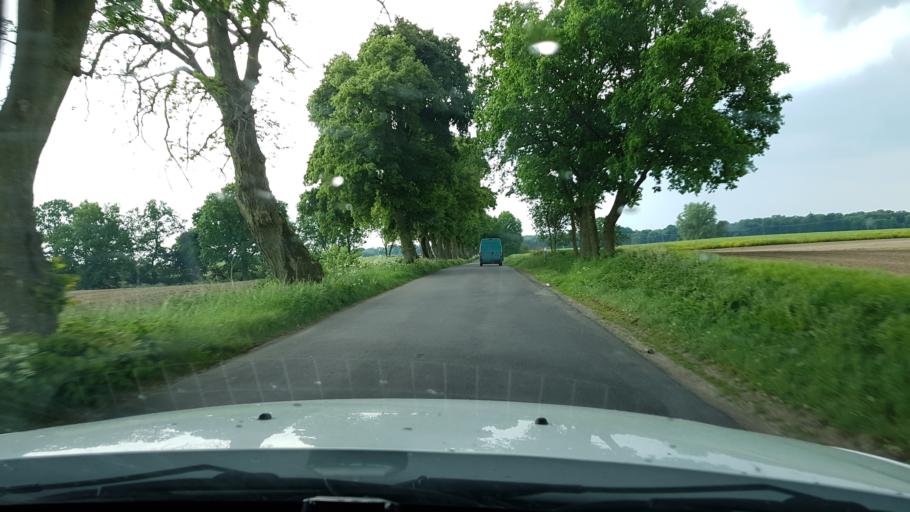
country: PL
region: West Pomeranian Voivodeship
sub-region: Powiat stargardzki
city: Marianowo
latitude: 53.3093
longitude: 15.1769
